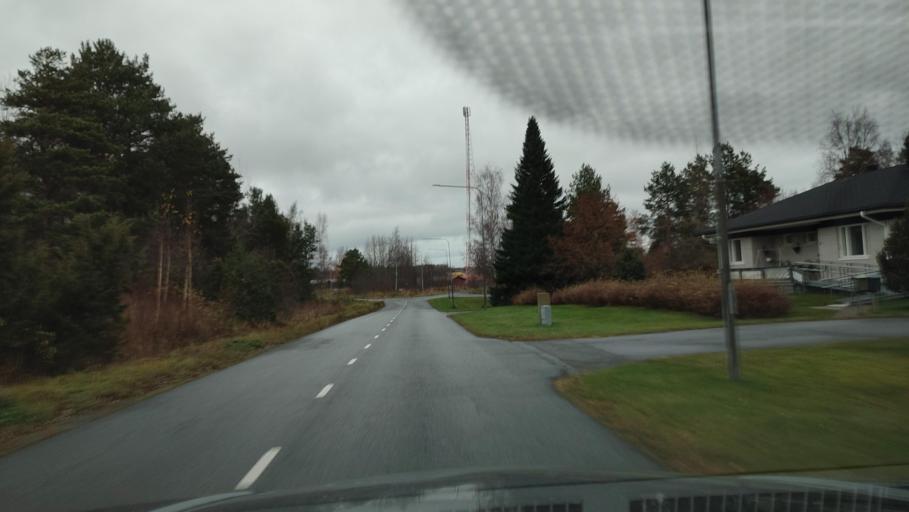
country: FI
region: Ostrobothnia
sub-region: Sydosterbotten
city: Kristinestad
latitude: 62.2754
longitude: 21.3998
